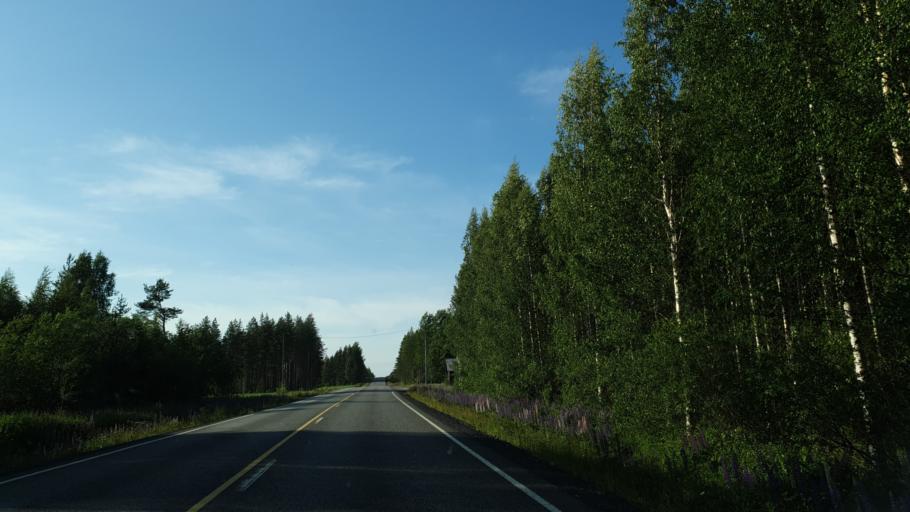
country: FI
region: Kainuu
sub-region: Kehys-Kainuu
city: Kuhmo
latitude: 64.0800
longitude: 29.4862
